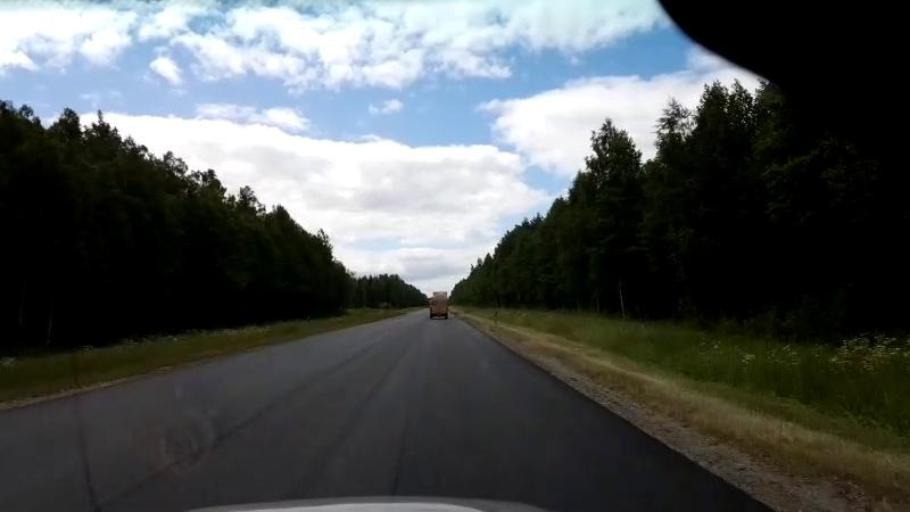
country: LV
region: Salacgrivas
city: Ainazi
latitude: 57.9225
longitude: 24.4235
